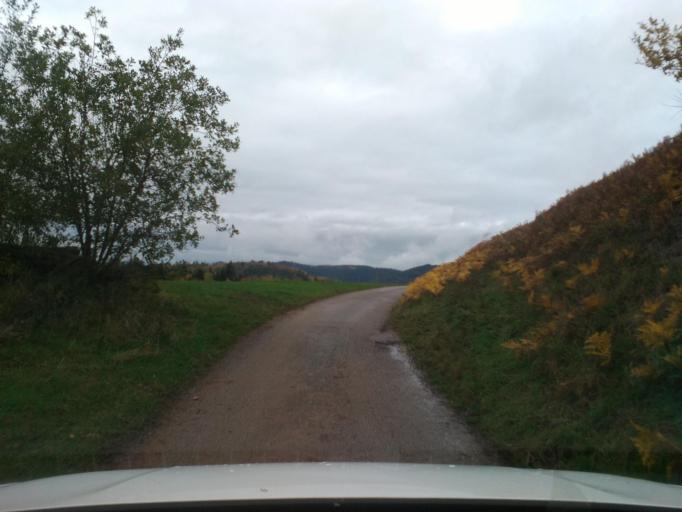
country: FR
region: Lorraine
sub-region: Departement des Vosges
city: Senones
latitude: 48.3808
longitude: 6.9903
